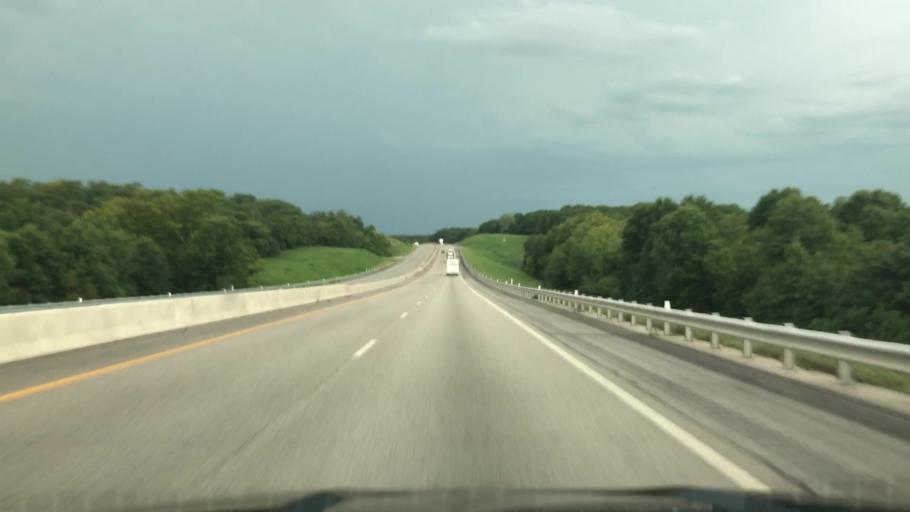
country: US
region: Oklahoma
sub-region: Rogers County
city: Justice
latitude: 36.3398
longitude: -95.4997
